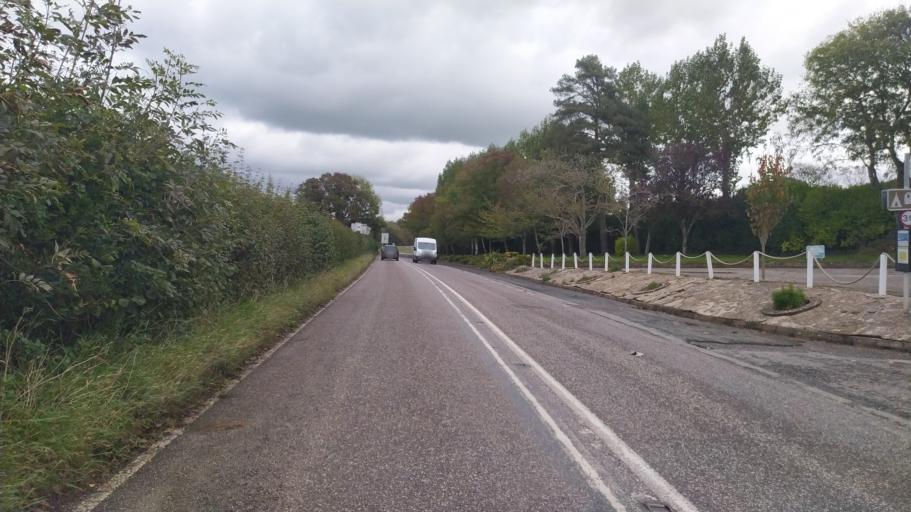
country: GB
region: England
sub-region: Dorset
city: Lyme Regis
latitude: 50.7391
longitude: -2.8902
